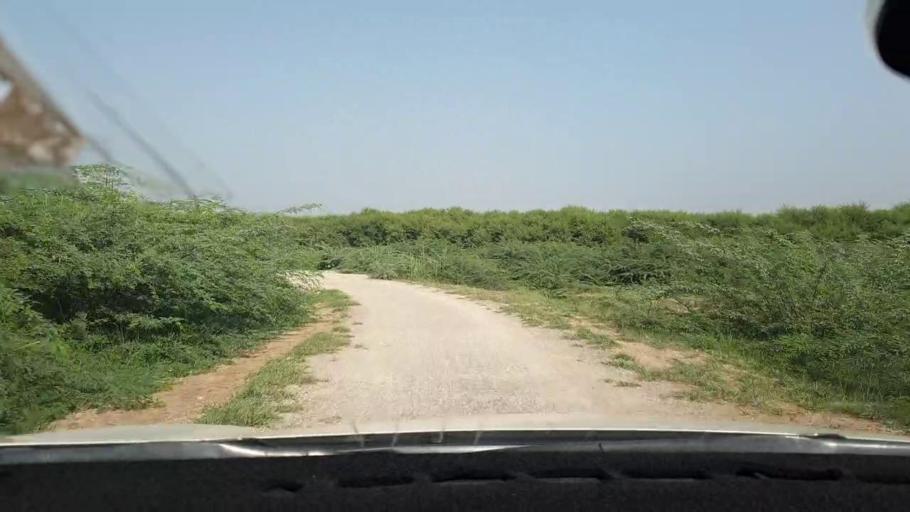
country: PK
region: Sindh
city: Tando Mittha Khan
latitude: 25.9442
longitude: 69.2990
